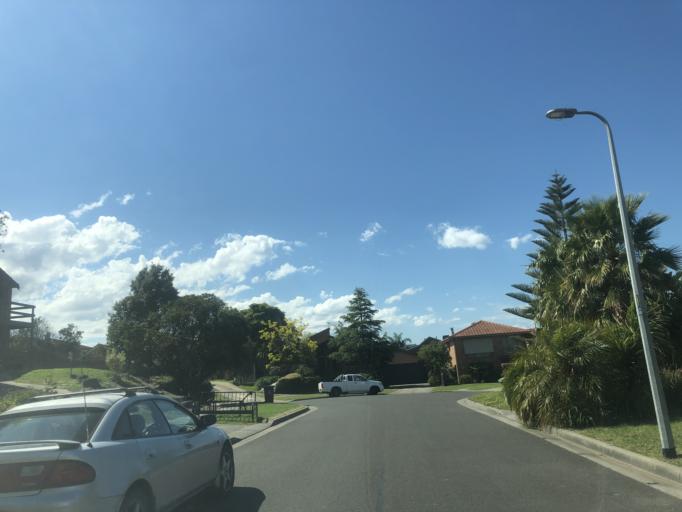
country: AU
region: Victoria
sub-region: Casey
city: Endeavour Hills
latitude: -37.9827
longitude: 145.2690
